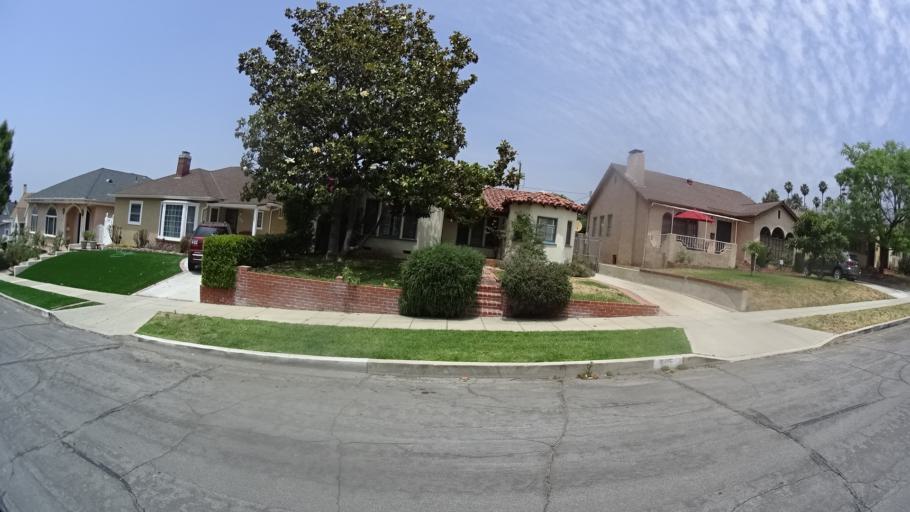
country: US
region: California
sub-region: Los Angeles County
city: Burbank
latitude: 34.1951
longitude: -118.3076
